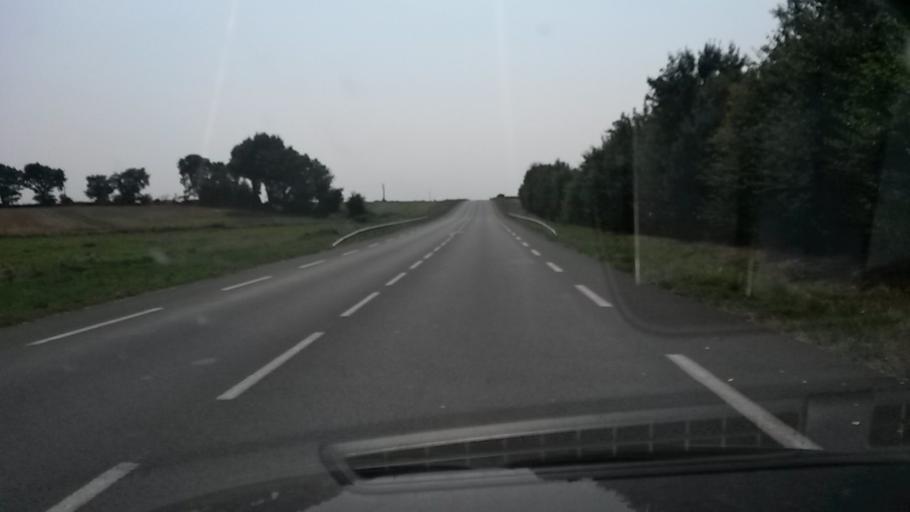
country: FR
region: Pays de la Loire
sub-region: Departement de la Mayenne
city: Chemaze
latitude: 47.7670
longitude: -0.7840
